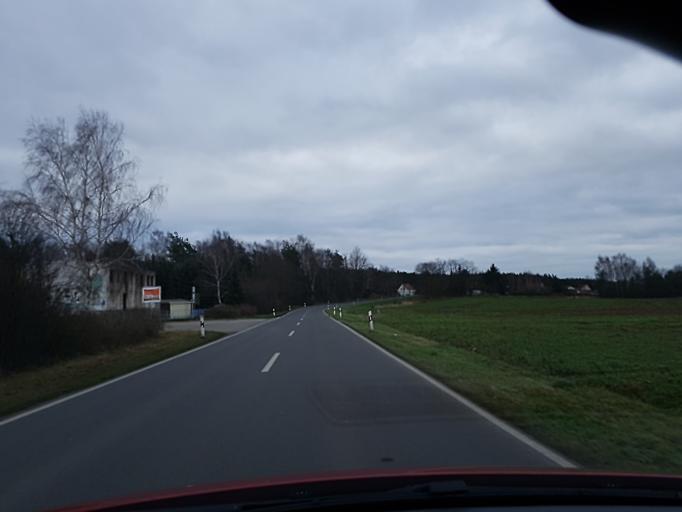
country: DE
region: Brandenburg
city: Bad Liebenwerda
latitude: 51.5555
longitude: 13.4210
